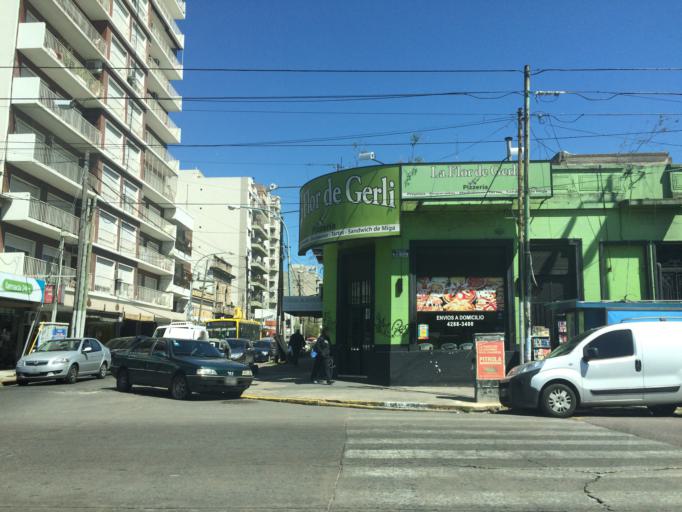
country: AR
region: Buenos Aires
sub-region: Partido de Lanus
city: Lanus
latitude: -34.7273
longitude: -58.3958
